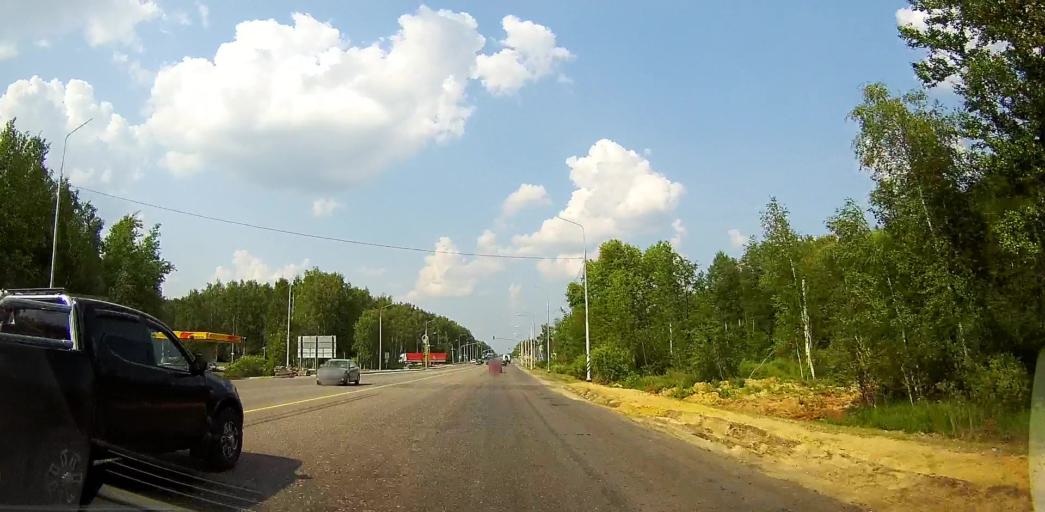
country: RU
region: Moskovskaya
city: Mikhnevo
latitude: 55.0754
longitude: 37.9516
